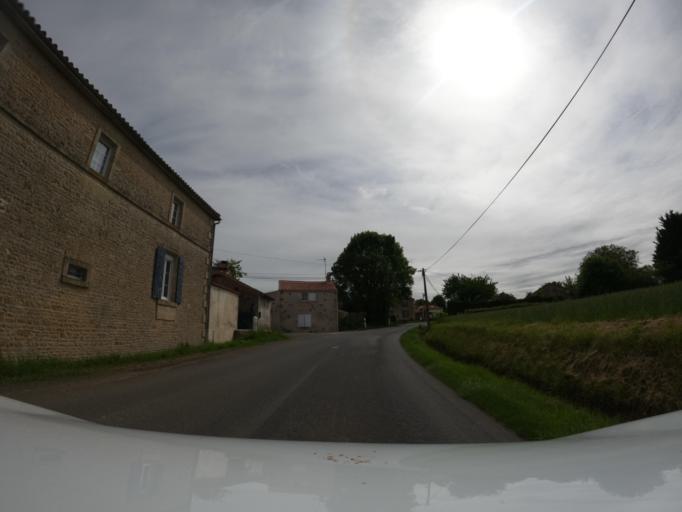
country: FR
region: Pays de la Loire
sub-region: Departement de la Vendee
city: Saint-Hilaire-des-Loges
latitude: 46.4995
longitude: -0.6517
